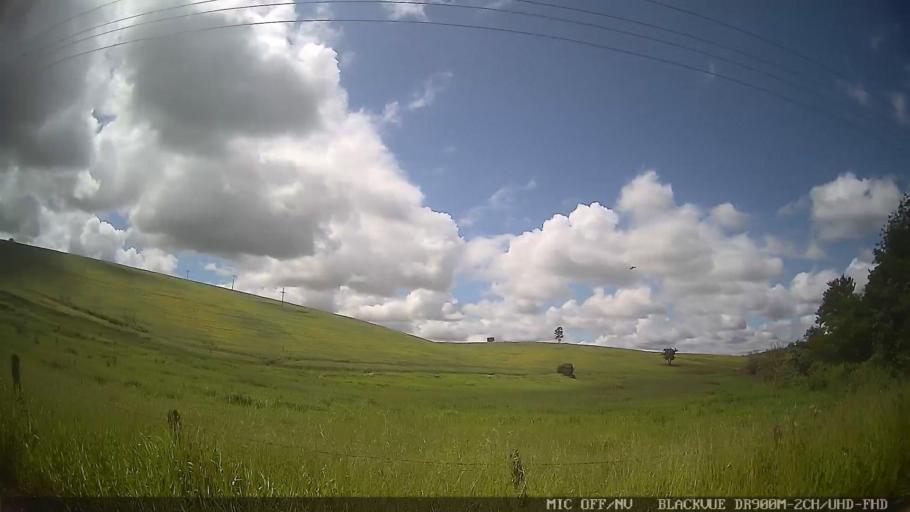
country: BR
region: Sao Paulo
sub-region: Braganca Paulista
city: Braganca Paulista
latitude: -22.8610
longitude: -46.6537
